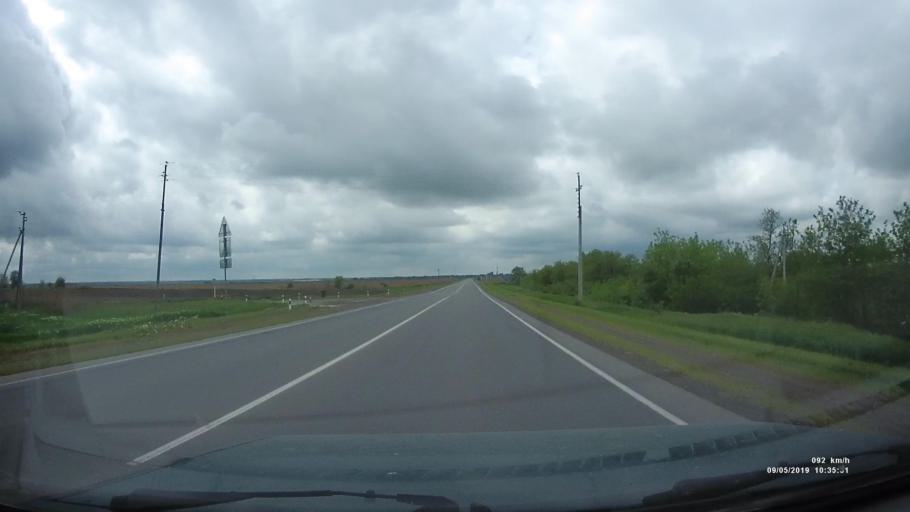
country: RU
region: Rostov
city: Peshkovo
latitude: 47.0416
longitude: 39.4132
